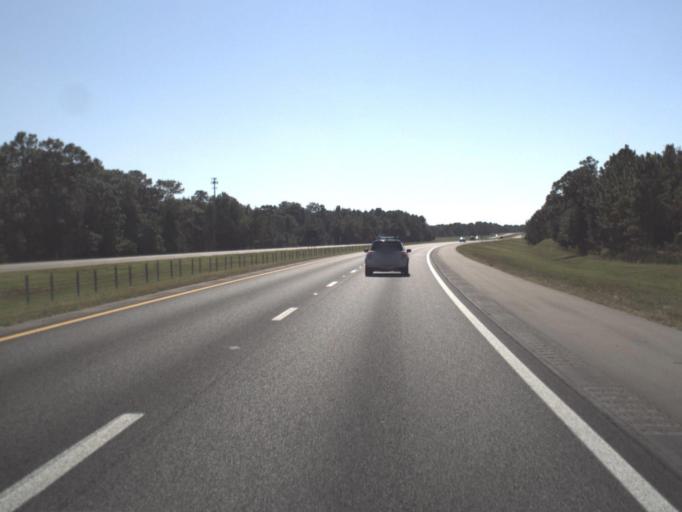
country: US
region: Florida
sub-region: Hernando County
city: Brookridge
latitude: 28.5156
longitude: -82.4773
